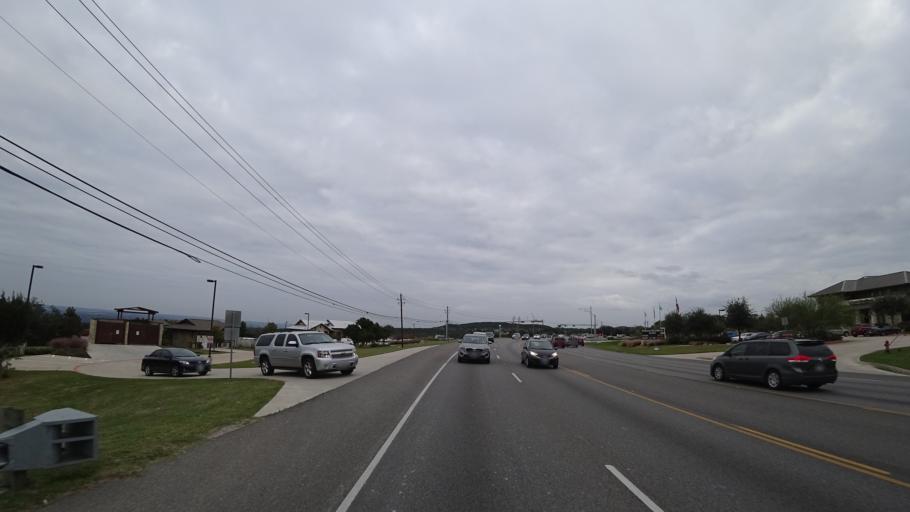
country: US
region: Texas
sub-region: Travis County
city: Bee Cave
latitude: 30.3256
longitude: -97.9596
